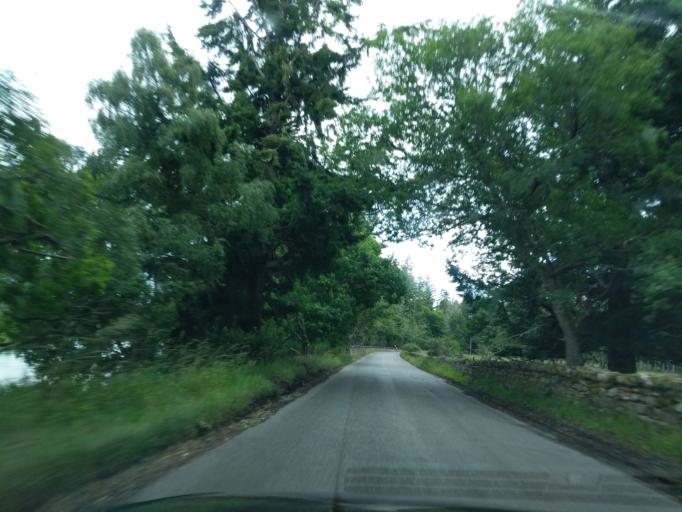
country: GB
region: Scotland
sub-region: Aberdeenshire
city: Aboyne
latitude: 57.0720
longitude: -2.8848
